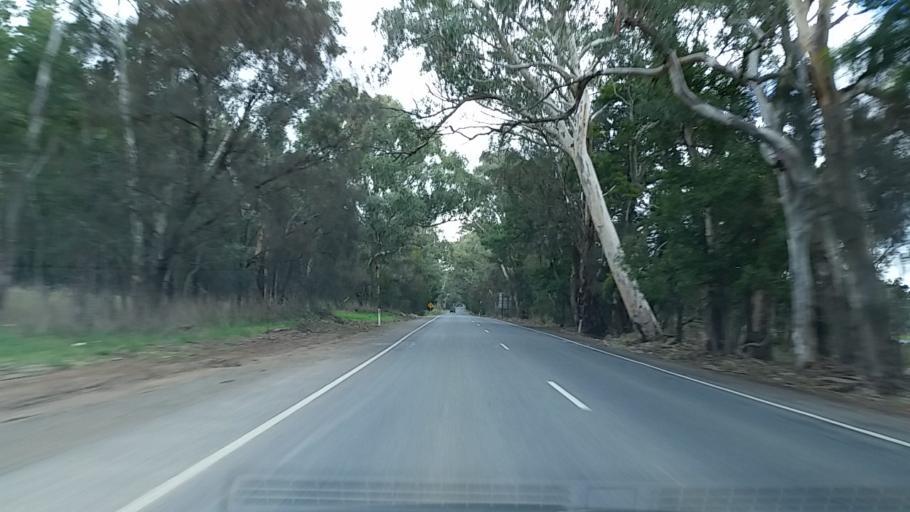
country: AU
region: South Australia
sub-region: Mount Barker
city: Meadows
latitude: -35.2331
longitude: 138.6811
